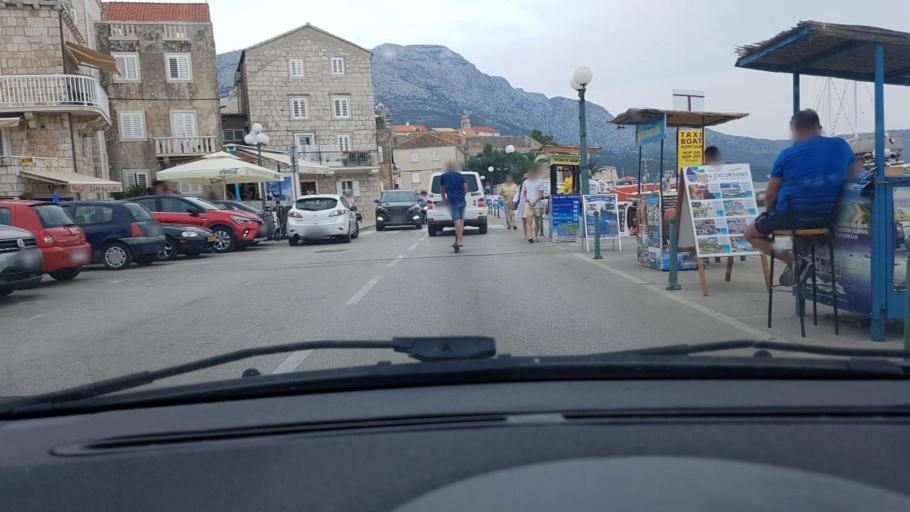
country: HR
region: Dubrovacko-Neretvanska
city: Korcula
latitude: 42.9595
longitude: 17.1354
